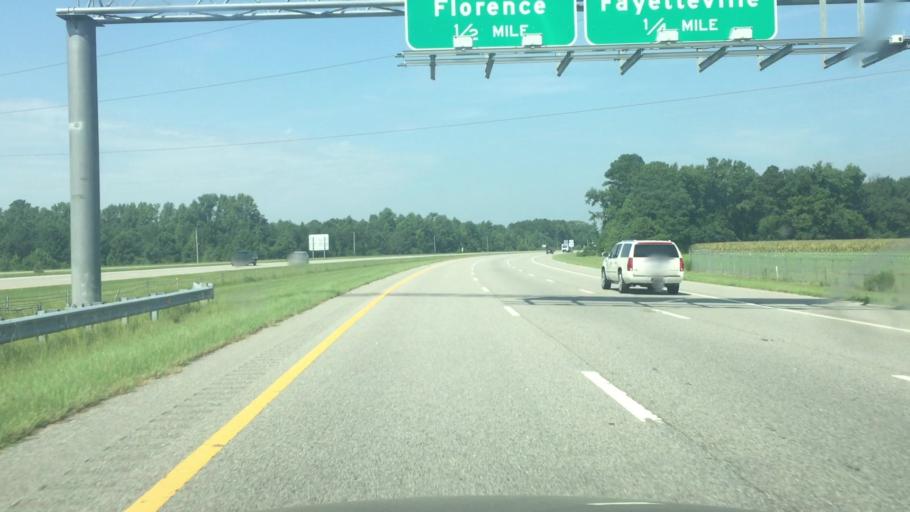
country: US
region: North Carolina
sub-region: Robeson County
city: Lumberton
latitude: 34.5917
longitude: -79.0950
